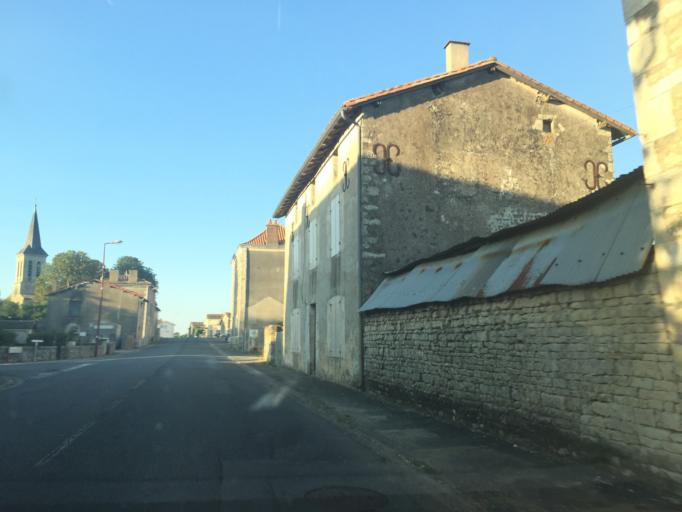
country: FR
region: Poitou-Charentes
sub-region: Departement des Deux-Sevres
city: Lezay
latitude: 46.3239
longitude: -0.0352
